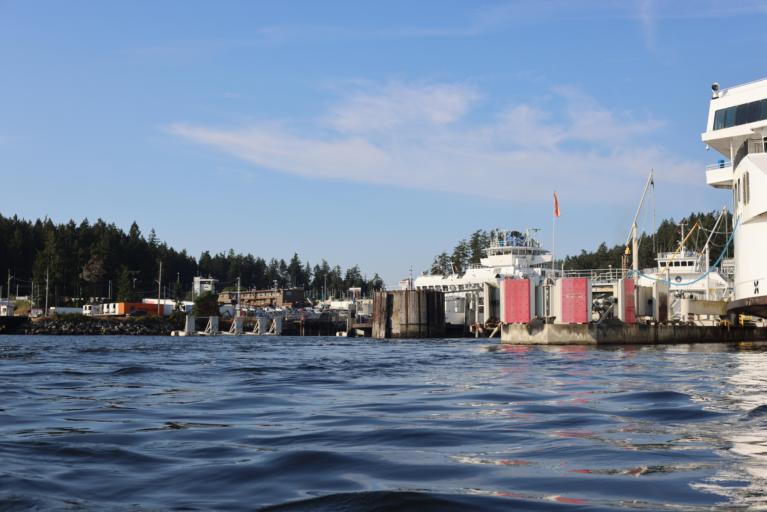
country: CA
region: British Columbia
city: North Saanich
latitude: 48.6908
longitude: -123.4087
